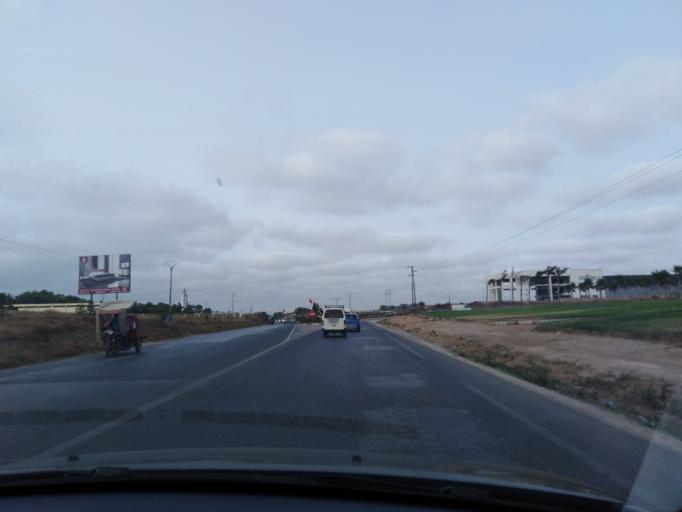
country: MA
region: Grand Casablanca
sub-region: Nouaceur
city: Bouskoura
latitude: 33.5095
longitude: -7.7046
